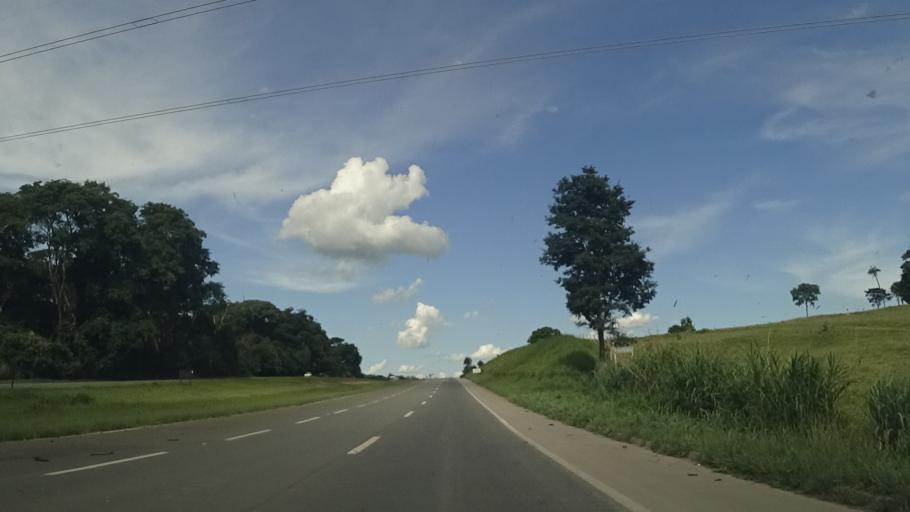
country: BR
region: Goias
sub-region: Piracanjuba
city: Piracanjuba
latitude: -17.2116
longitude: -49.2219
